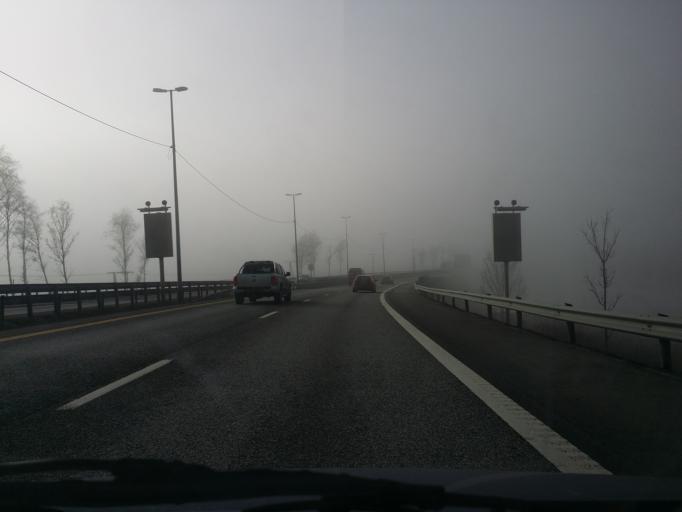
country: NO
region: Buskerud
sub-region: Lier
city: Lierbyen
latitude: 59.7768
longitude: 10.2764
